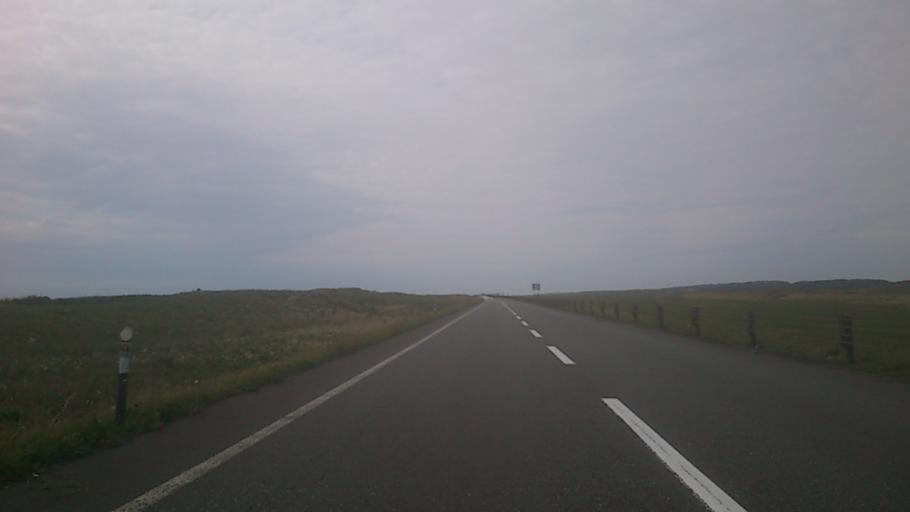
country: JP
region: Hokkaido
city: Wakkanai
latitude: 45.0616
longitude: 141.6464
